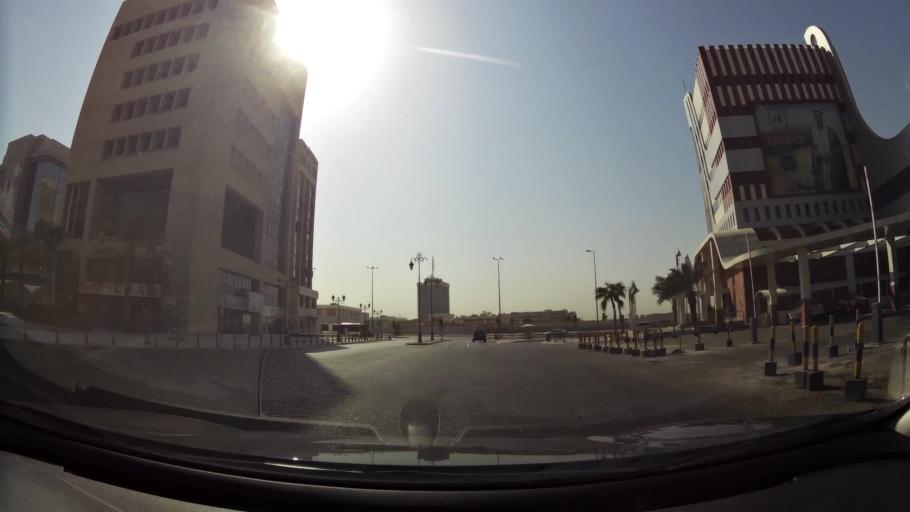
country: KW
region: Al Asimah
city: Kuwait City
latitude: 29.3669
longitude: 47.9704
